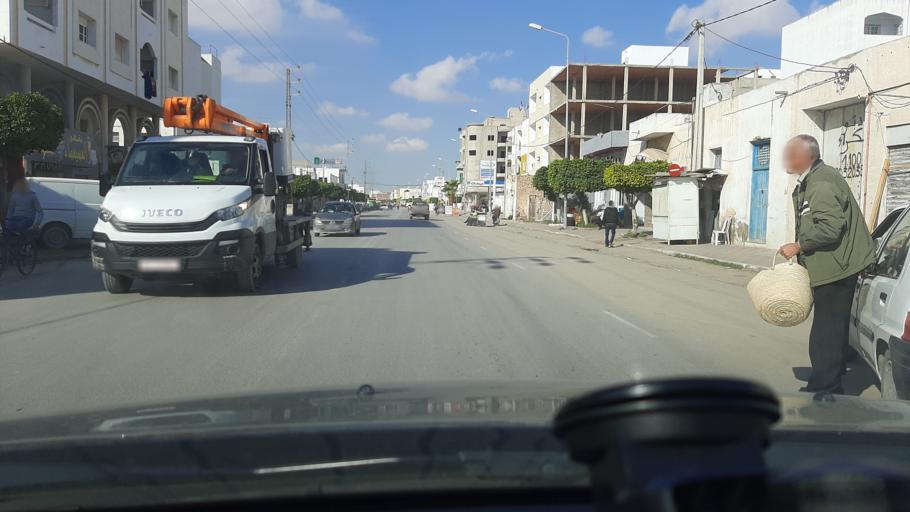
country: TN
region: Safaqis
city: Sfax
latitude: 34.7944
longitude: 10.7145
